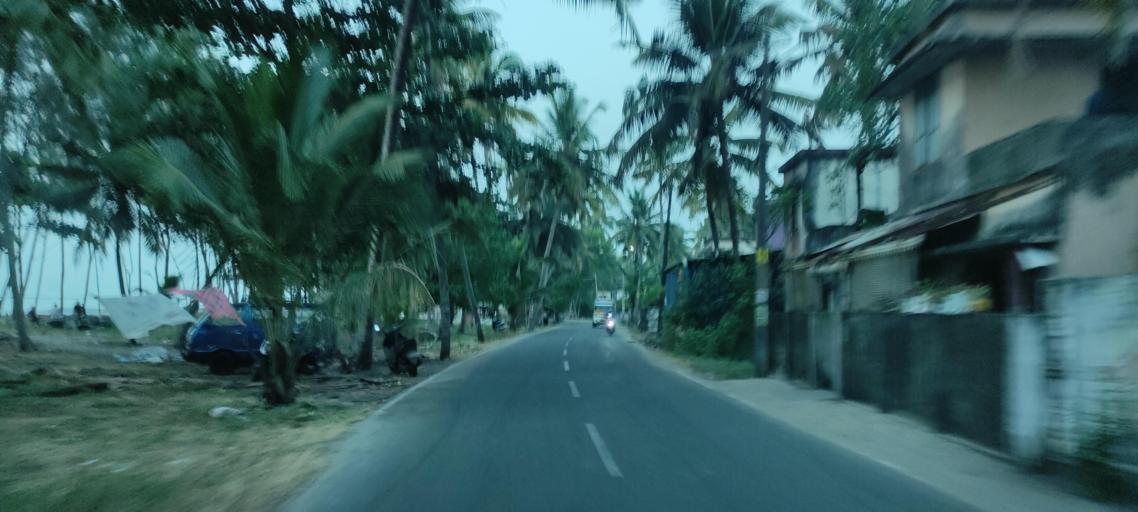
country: IN
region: Kerala
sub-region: Alappuzha
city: Kayankulam
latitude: 9.1291
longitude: 76.4663
